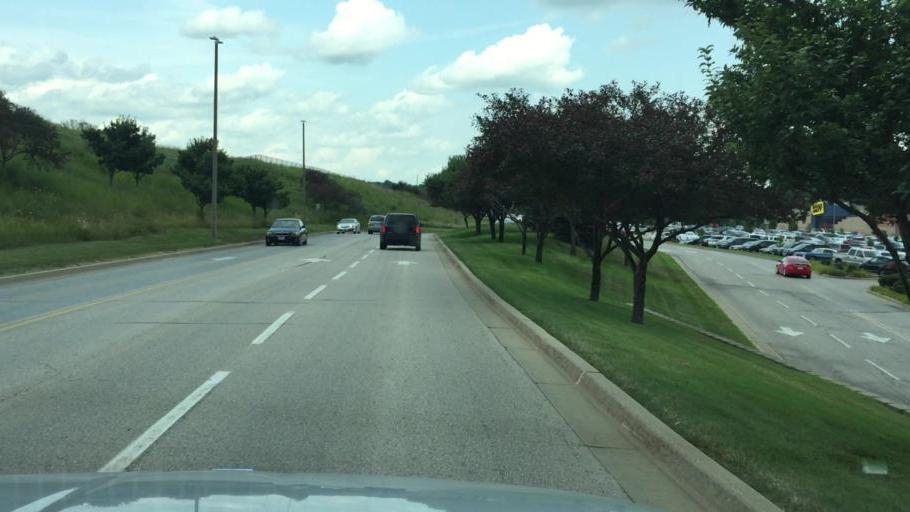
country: US
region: Iowa
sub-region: Johnson County
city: Coralville
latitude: 41.6932
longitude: -91.6023
